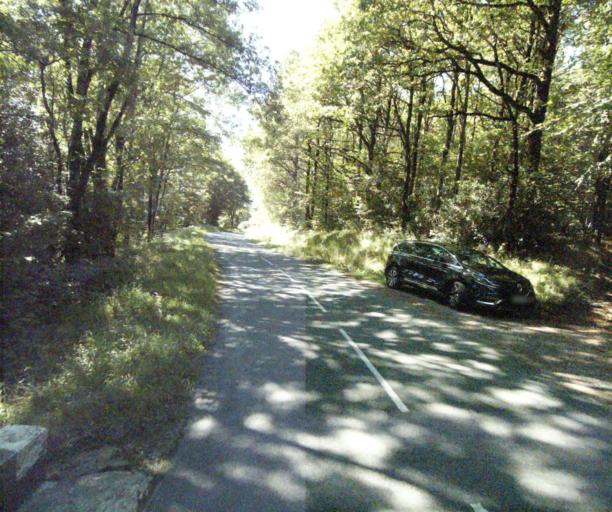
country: FR
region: Midi-Pyrenees
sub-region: Departement du Tarn
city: Soreze
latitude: 43.4338
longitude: 2.1125
